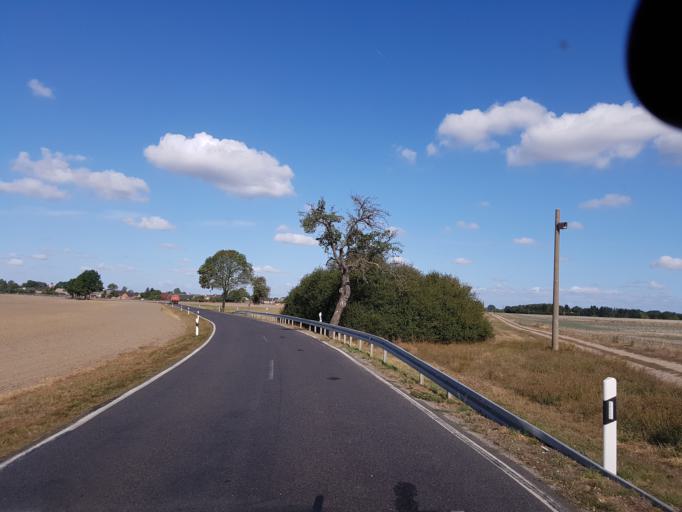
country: DE
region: Brandenburg
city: Sonnewalde
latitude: 51.7066
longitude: 13.6432
